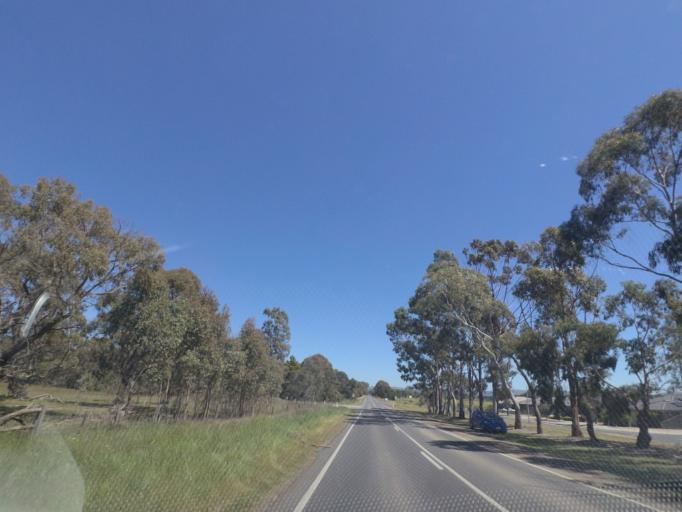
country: AU
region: Victoria
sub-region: Whittlesea
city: Whittlesea
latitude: -37.2936
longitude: 144.9296
